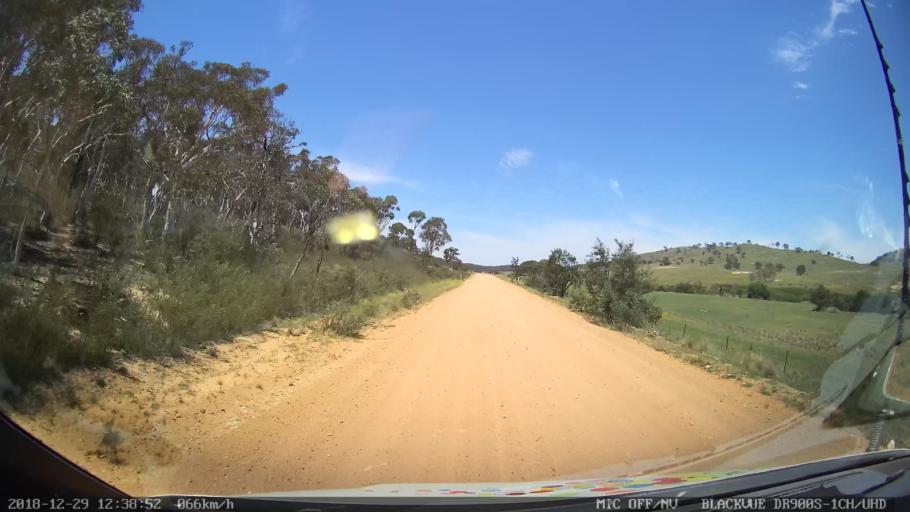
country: AU
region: Australian Capital Territory
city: Macarthur
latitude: -35.5926
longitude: 149.2283
